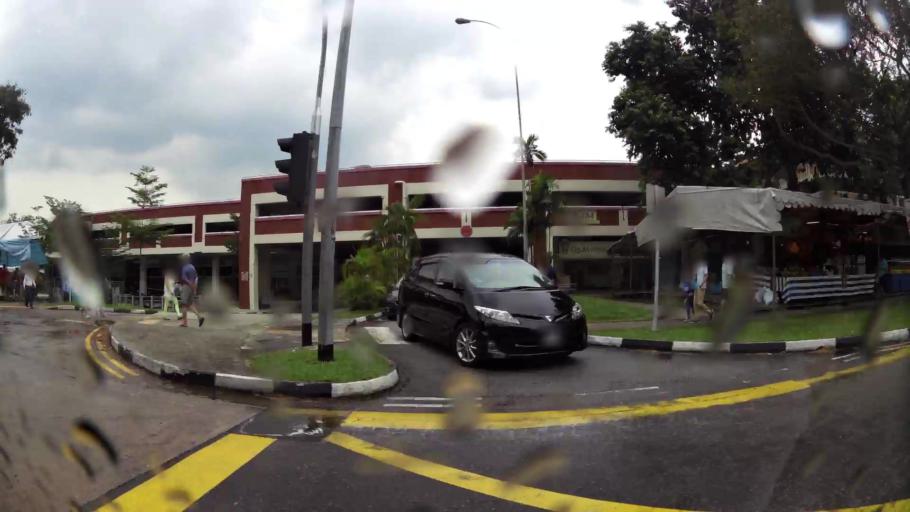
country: SG
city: Singapore
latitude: 1.3528
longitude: 103.8726
